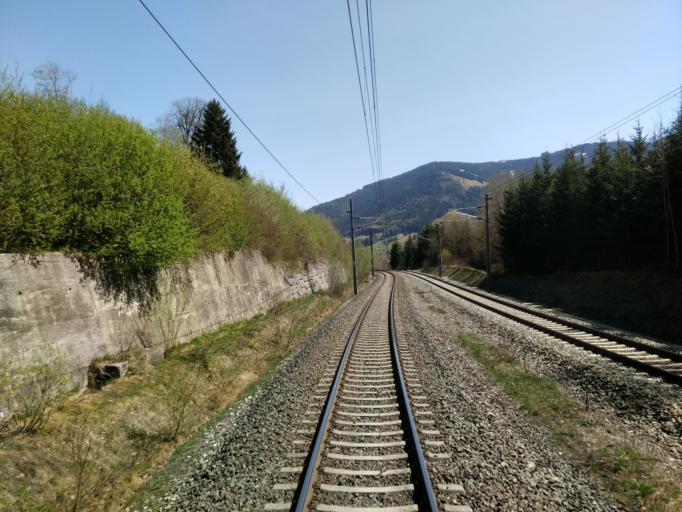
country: AT
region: Salzburg
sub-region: Politischer Bezirk Zell am See
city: Leogang
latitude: 47.4430
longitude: 12.7431
